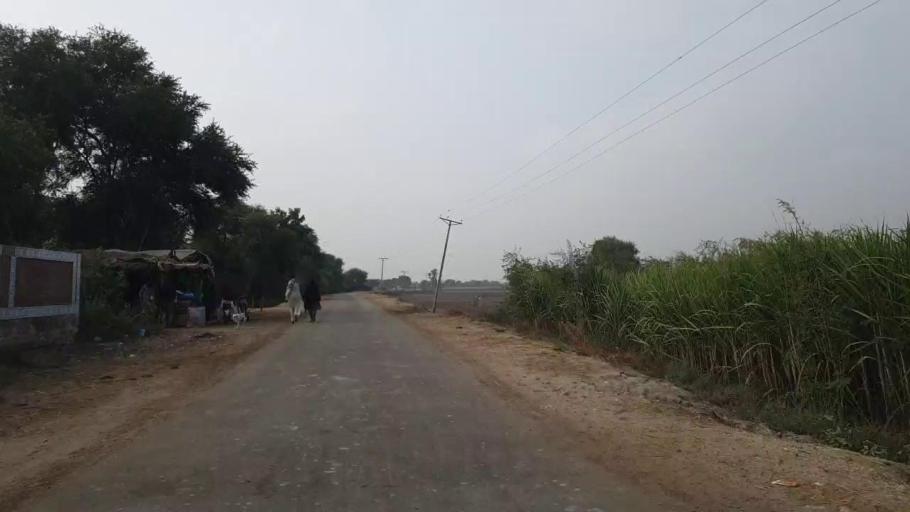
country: PK
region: Sindh
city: Matli
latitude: 24.9848
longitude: 68.6264
